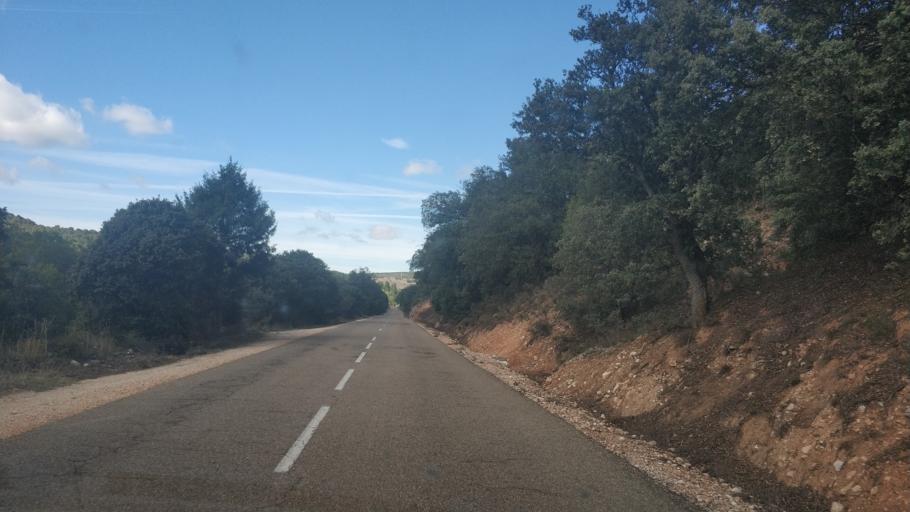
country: ES
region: Castille and Leon
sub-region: Provincia de Burgos
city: Covarrubias
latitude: 42.0521
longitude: -3.4977
